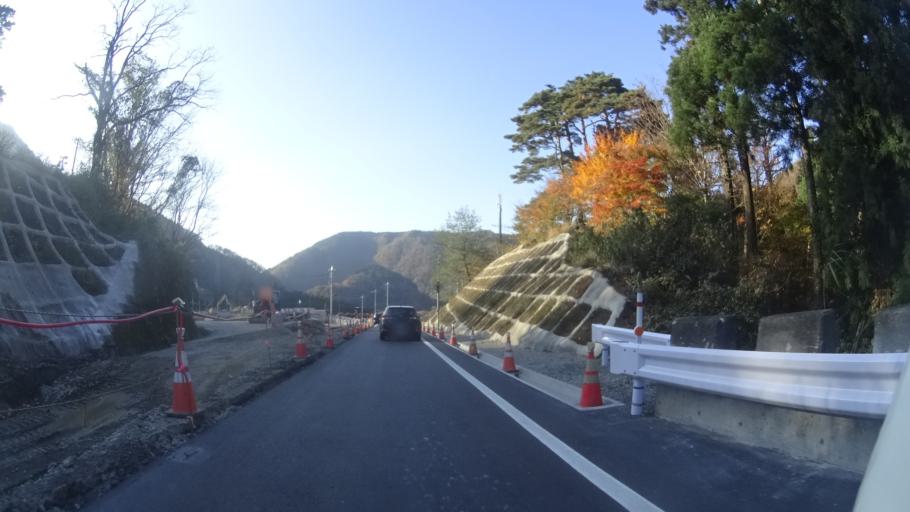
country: JP
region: Fukui
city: Ono
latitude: 35.9642
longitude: 136.6055
